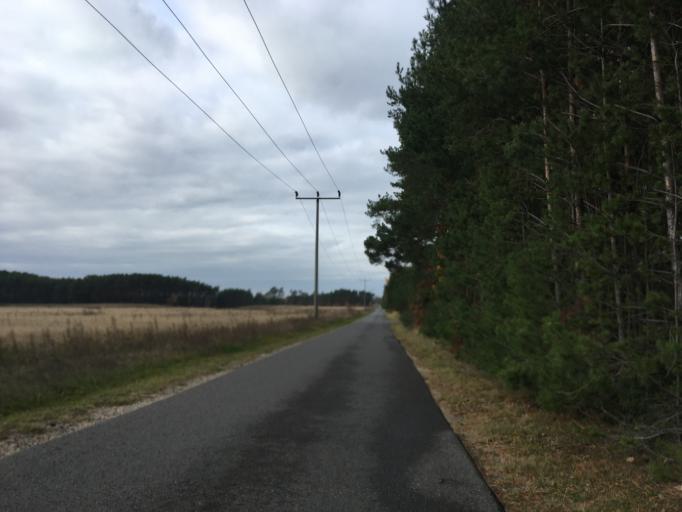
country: DE
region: Brandenburg
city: Jamlitz
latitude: 52.0808
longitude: 14.4522
